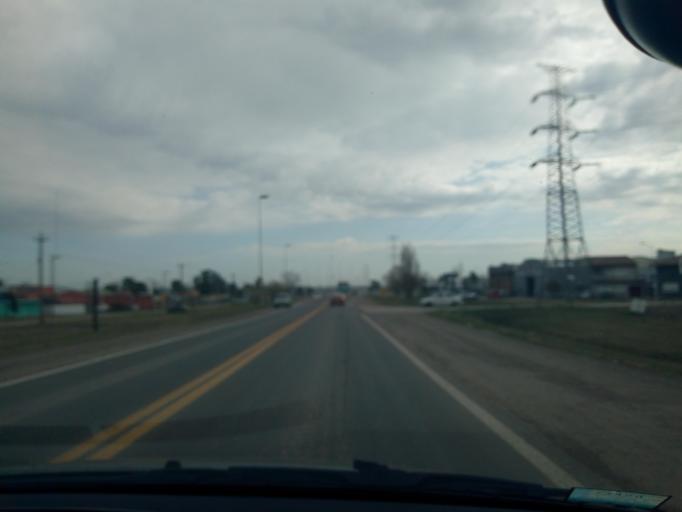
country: AR
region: Buenos Aires
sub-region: Partido de Tandil
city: Tandil
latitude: -37.3213
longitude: -59.1015
